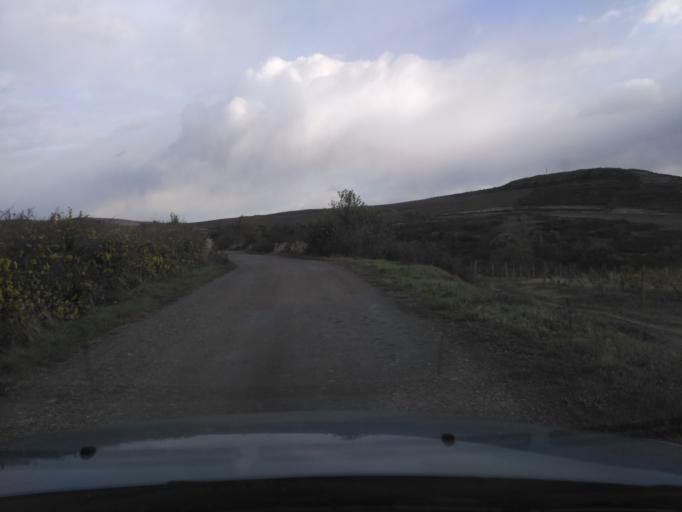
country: HU
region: Borsod-Abauj-Zemplen
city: Satoraljaujhely
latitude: 48.4428
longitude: 21.6919
